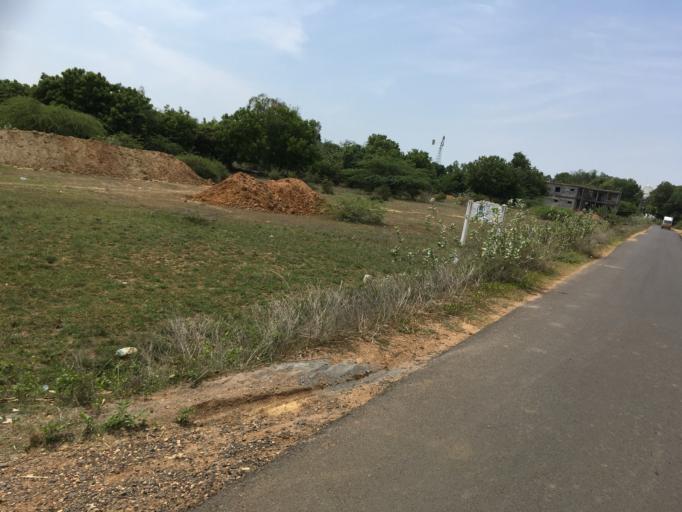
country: IN
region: Tamil Nadu
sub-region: Villupuram
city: Auroville
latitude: 12.0080
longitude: 79.7962
